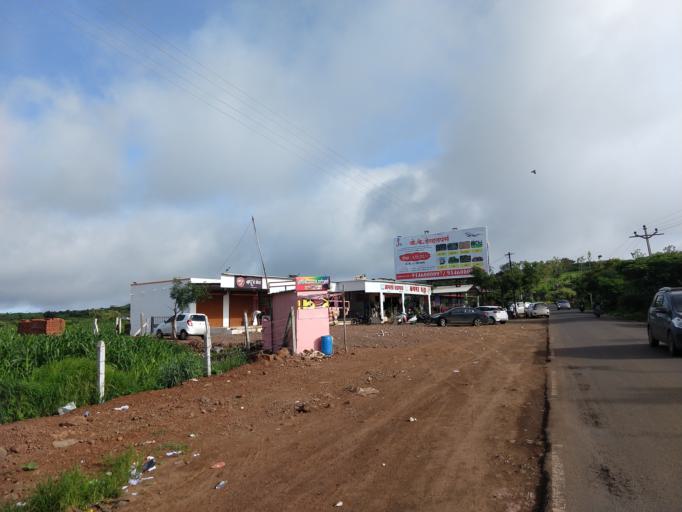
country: IN
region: Maharashtra
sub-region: Pune Division
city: Khed
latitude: 18.4019
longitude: 73.9120
